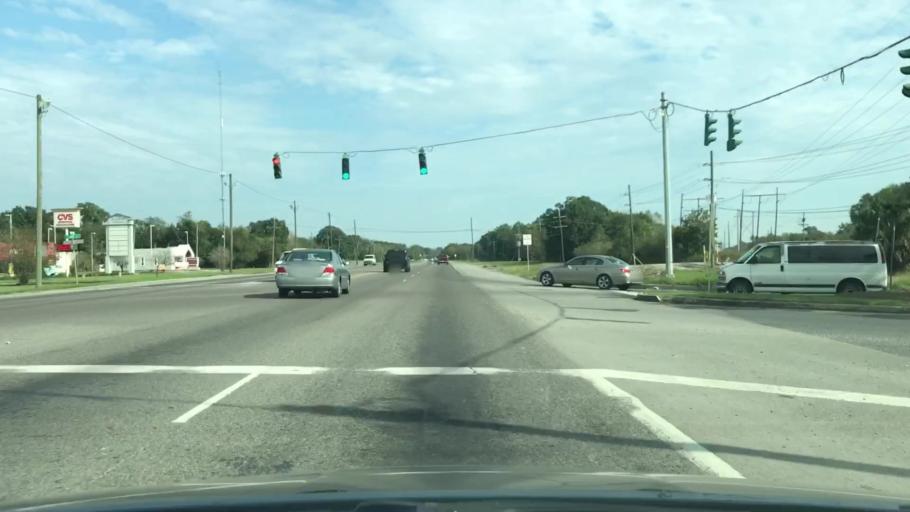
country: US
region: Louisiana
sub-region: Jefferson Parish
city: Avondale
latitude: 29.9099
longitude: -90.2031
